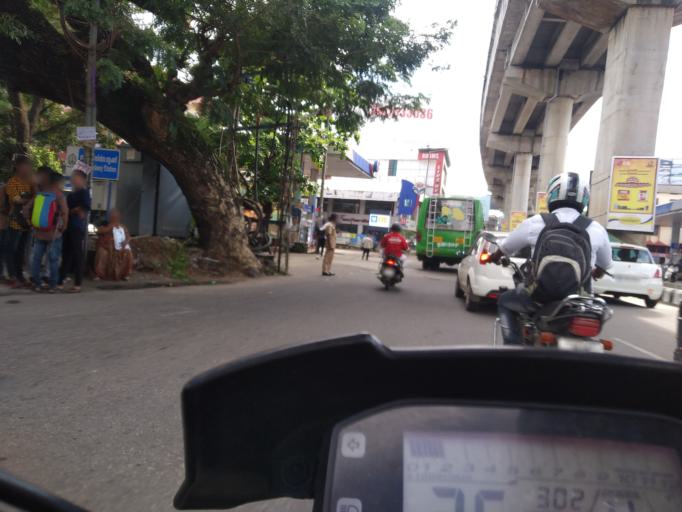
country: IN
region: Kerala
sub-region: Ernakulam
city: Cochin
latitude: 9.9883
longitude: 76.2860
